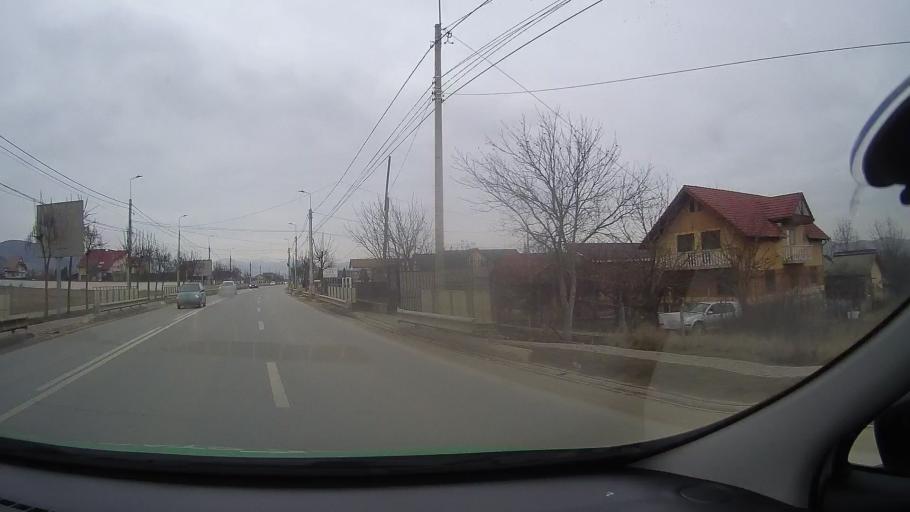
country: RO
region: Alba
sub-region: Municipiul Alba Iulia
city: Micesti
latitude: 46.0960
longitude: 23.5528
